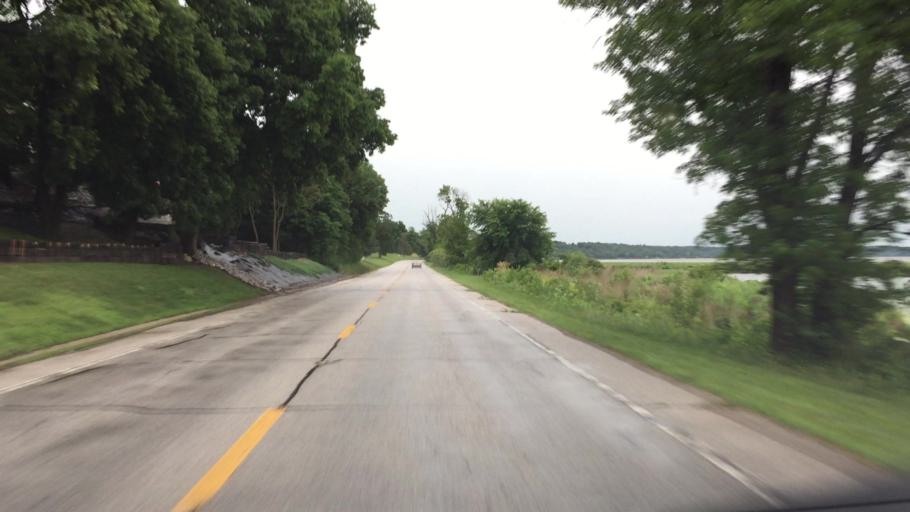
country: US
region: Illinois
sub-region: Hancock County
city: Nauvoo
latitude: 40.5304
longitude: -91.3730
